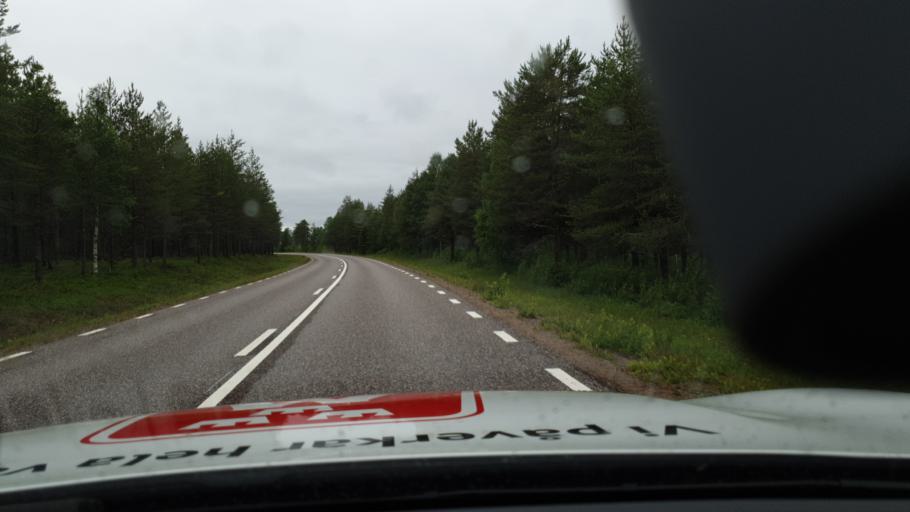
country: SE
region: Norrbotten
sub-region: Pajala Kommun
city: Pajala
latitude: 67.1951
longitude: 23.4605
